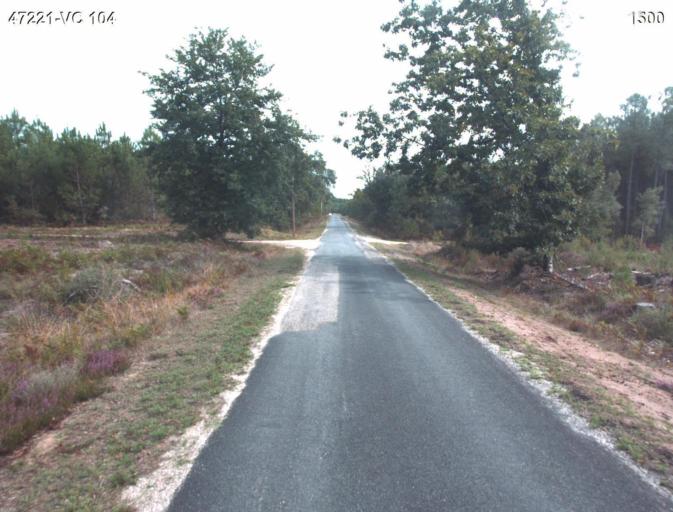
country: FR
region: Aquitaine
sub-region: Departement du Lot-et-Garonne
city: Mezin
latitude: 44.1255
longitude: 0.2100
